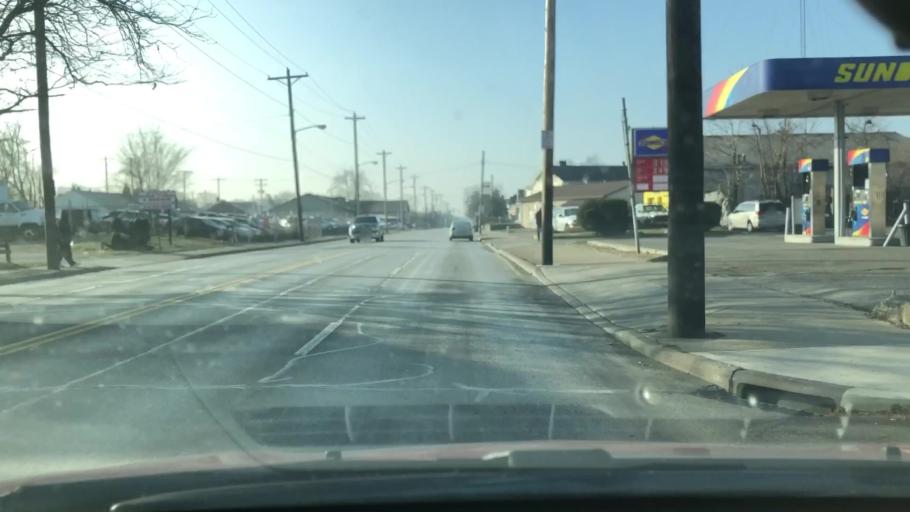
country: US
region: Ohio
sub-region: Franklin County
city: Bexley
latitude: 40.0054
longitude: -82.9725
